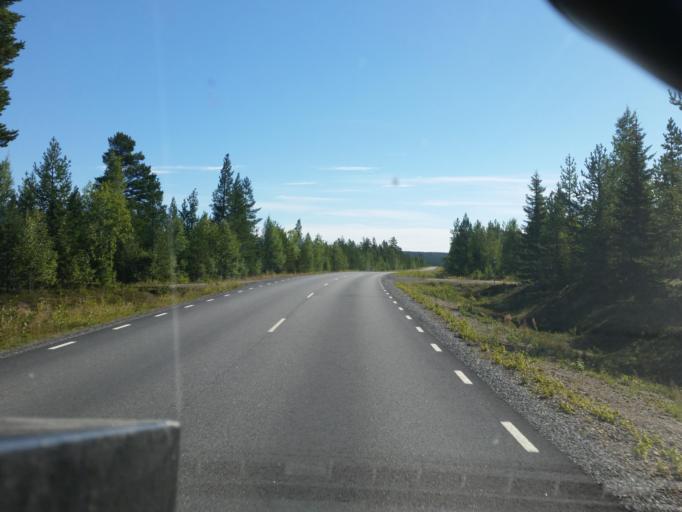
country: SE
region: Vaesterbotten
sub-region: Skelleftea Kommun
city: Storvik
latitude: 65.3284
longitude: 20.6641
